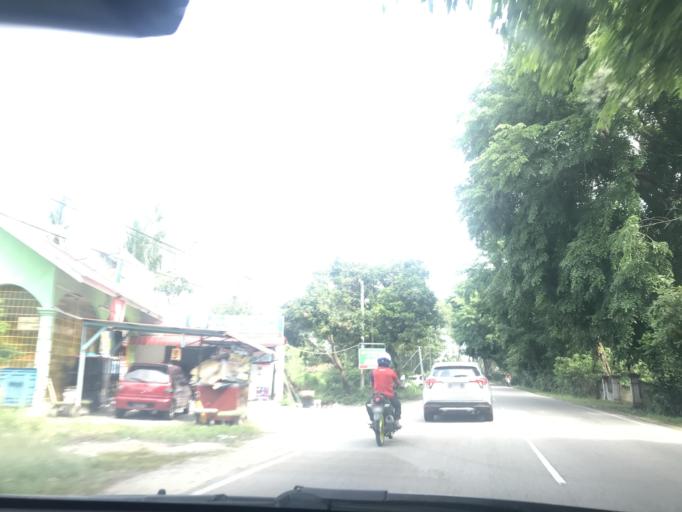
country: MY
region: Kelantan
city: Tumpat
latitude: 6.2135
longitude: 102.1293
